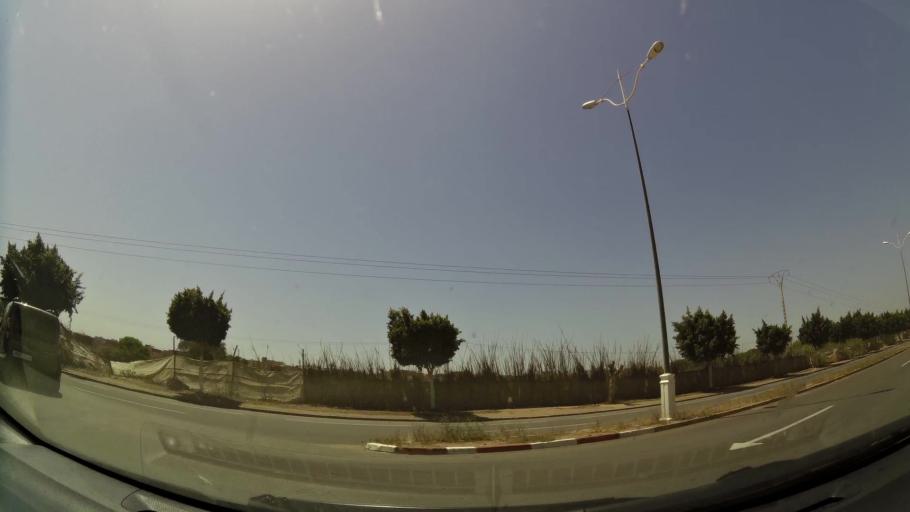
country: MA
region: Souss-Massa-Draa
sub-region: Inezgane-Ait Mellou
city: Inezgane
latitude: 30.3497
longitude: -9.4860
